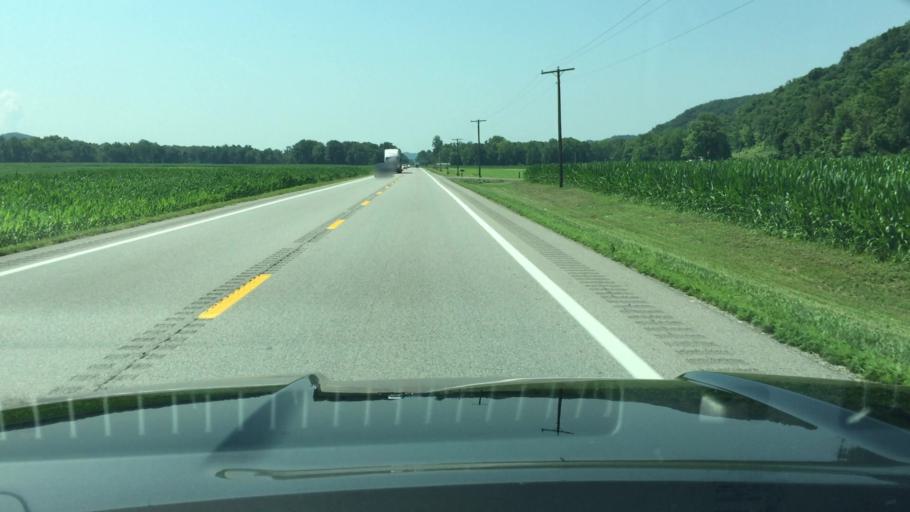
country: US
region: West Virginia
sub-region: Putnam County
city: Buffalo
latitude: 38.6982
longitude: -81.9661
